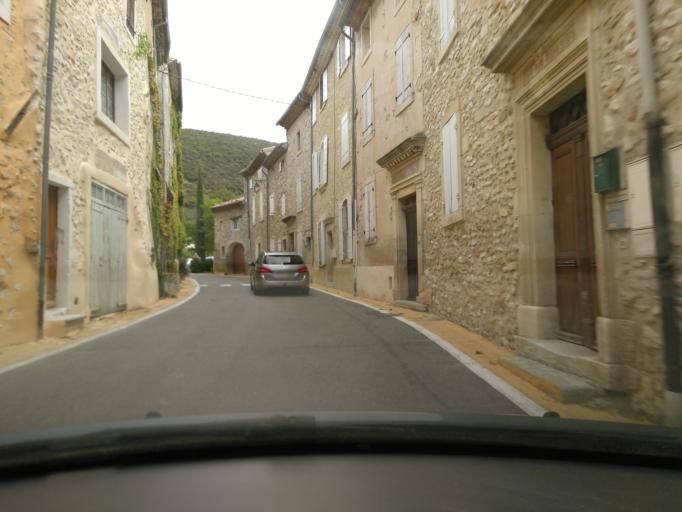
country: FR
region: Provence-Alpes-Cote d'Azur
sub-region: Departement du Vaucluse
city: Valreas
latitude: 44.4186
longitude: 5.0612
